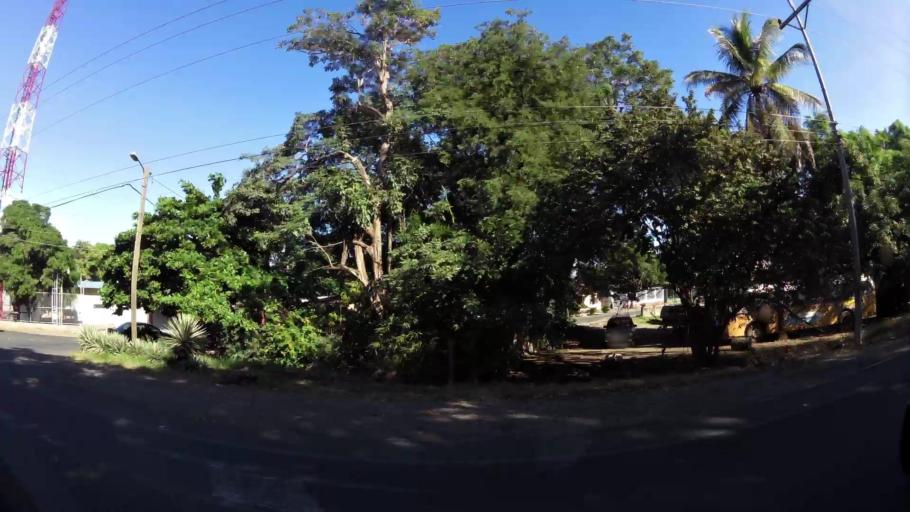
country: CR
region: Guanacaste
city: Sardinal
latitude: 10.5631
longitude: -85.5905
